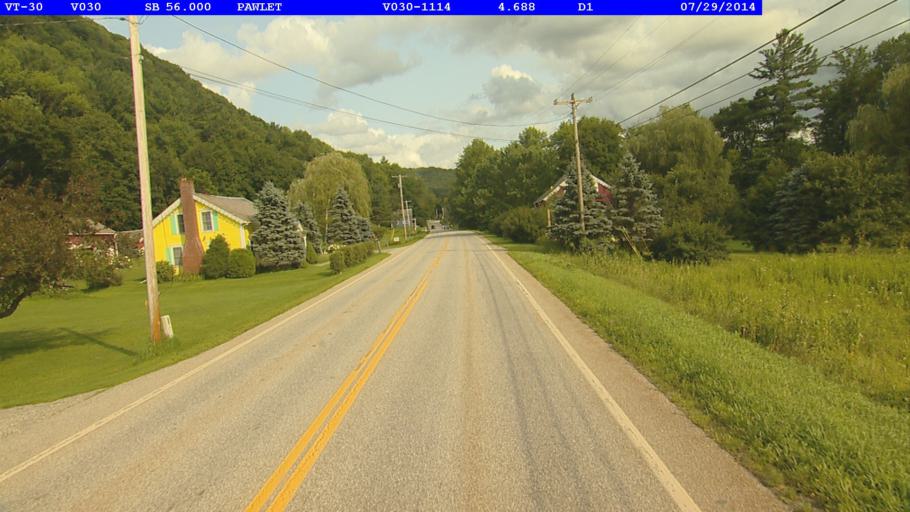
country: US
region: New York
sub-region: Washington County
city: Granville
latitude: 43.3729
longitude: -73.1906
